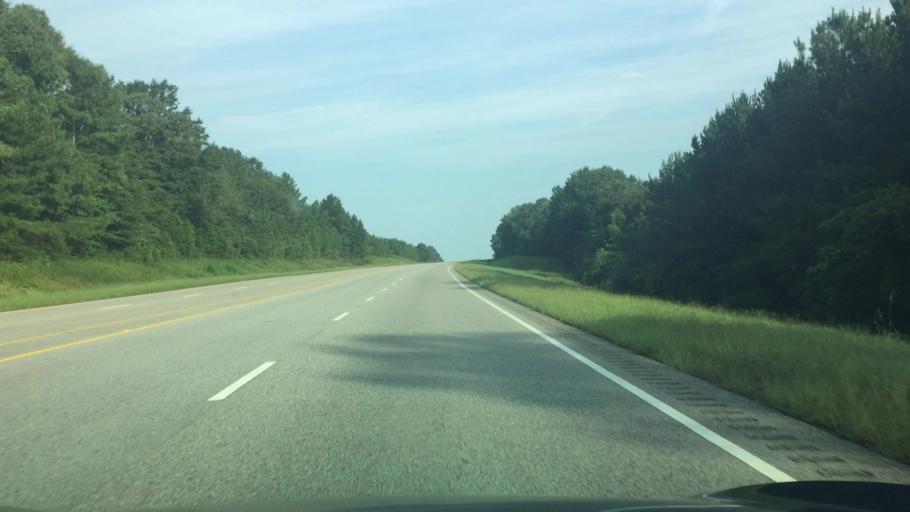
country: US
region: Alabama
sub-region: Covington County
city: Andalusia
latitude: 31.4505
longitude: -86.6266
